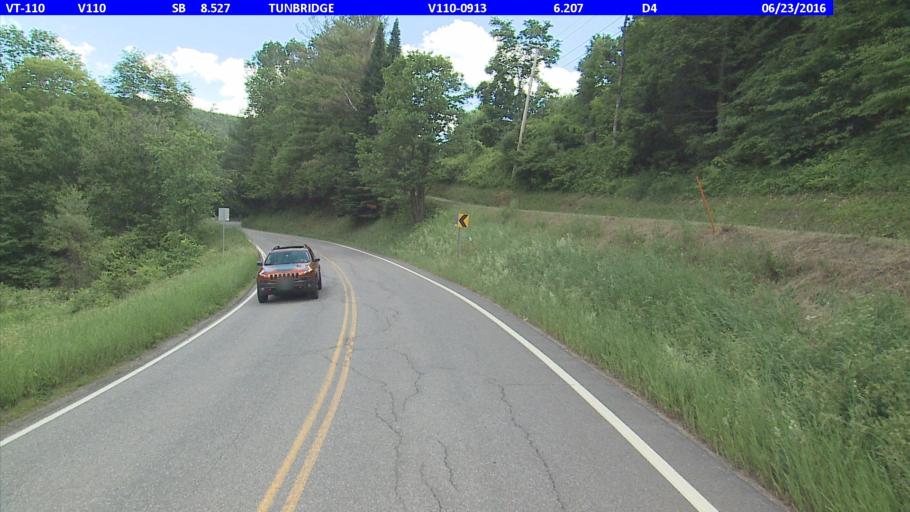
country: US
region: Vermont
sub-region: Orange County
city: Chelsea
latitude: 43.9289
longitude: -72.4666
